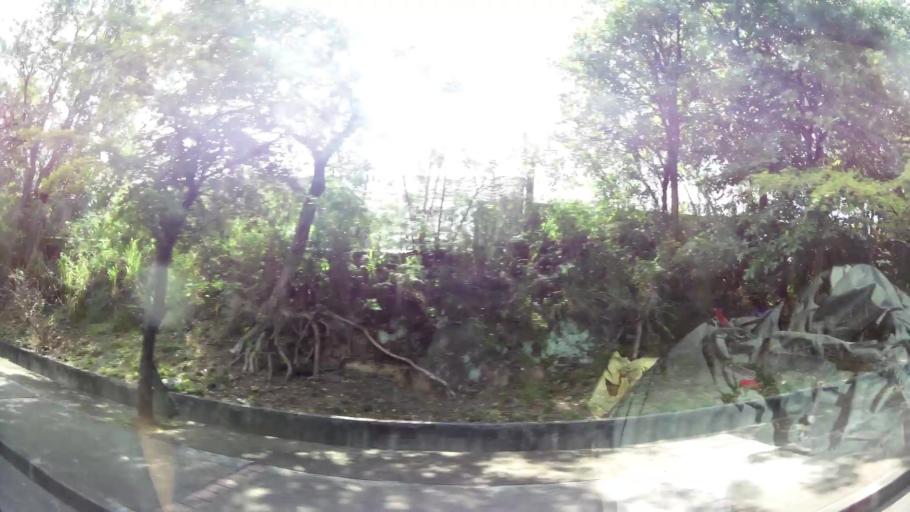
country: GP
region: Guadeloupe
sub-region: Guadeloupe
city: Basse-Terre
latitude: 16.0026
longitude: -61.7268
